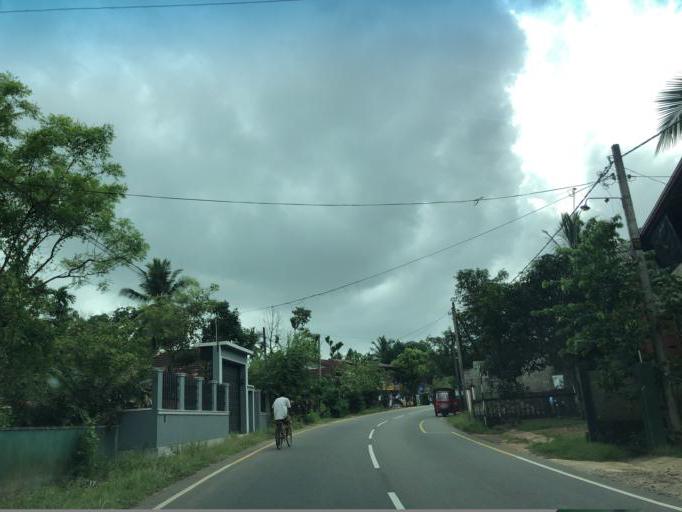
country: LK
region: Western
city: Horana South
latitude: 6.6822
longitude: 80.1057
